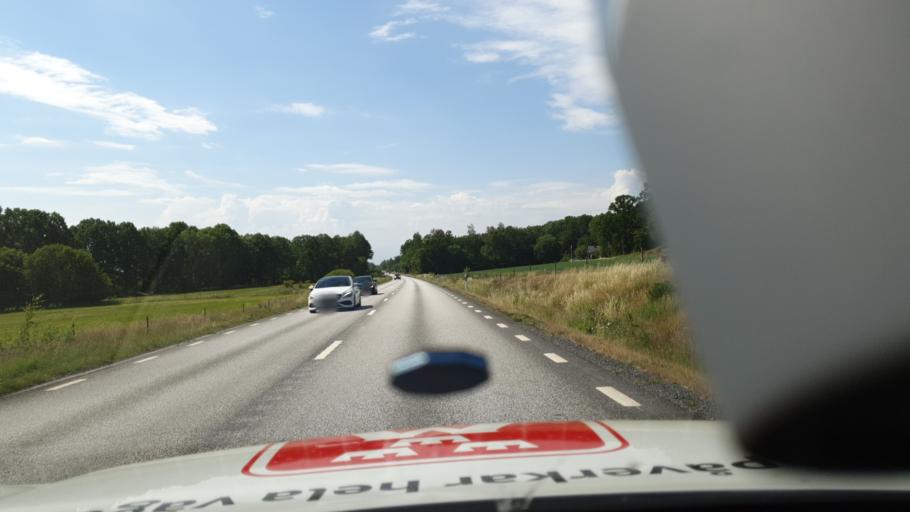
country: SE
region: Joenkoeping
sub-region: Habo Kommun
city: Habo
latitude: 58.0547
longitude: 14.1883
